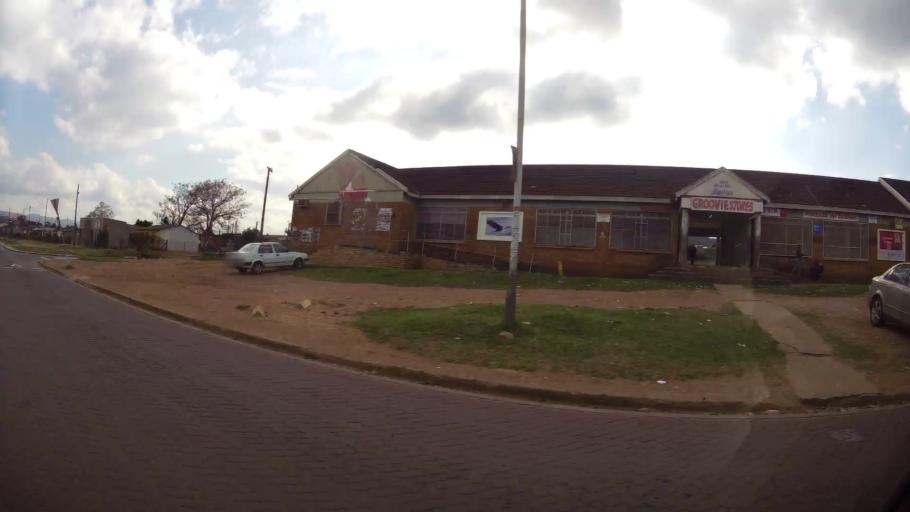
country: ZA
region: Eastern Cape
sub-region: Nelson Mandela Bay Metropolitan Municipality
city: Uitenhage
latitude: -33.7328
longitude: 25.3793
